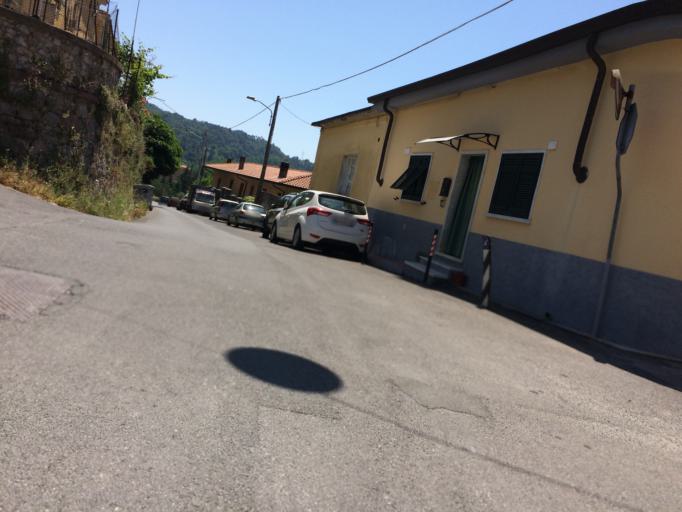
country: IT
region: Tuscany
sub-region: Provincia di Massa-Carrara
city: Carrara
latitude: 44.0769
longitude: 10.1106
